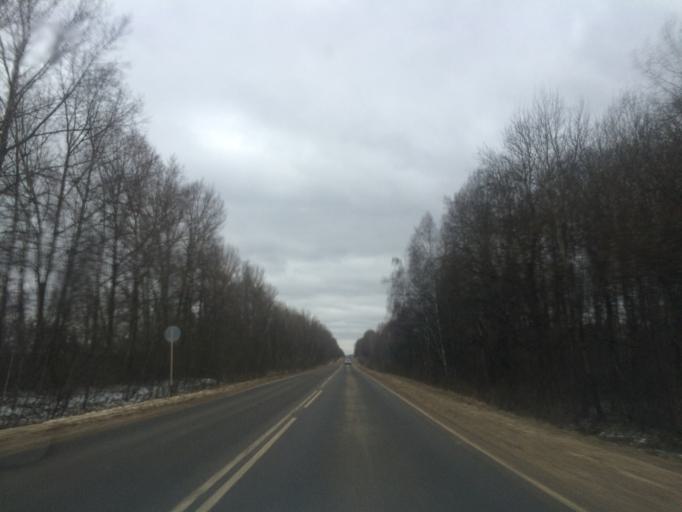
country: RU
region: Tula
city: Odoyev
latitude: 53.9714
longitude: 36.7180
